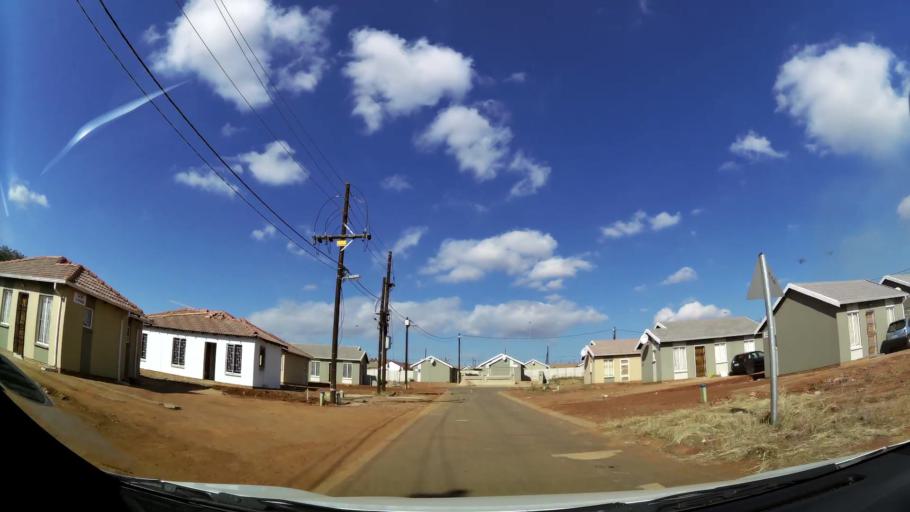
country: ZA
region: Gauteng
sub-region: City of Tshwane Metropolitan Municipality
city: Cullinan
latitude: -25.6854
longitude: 28.4110
